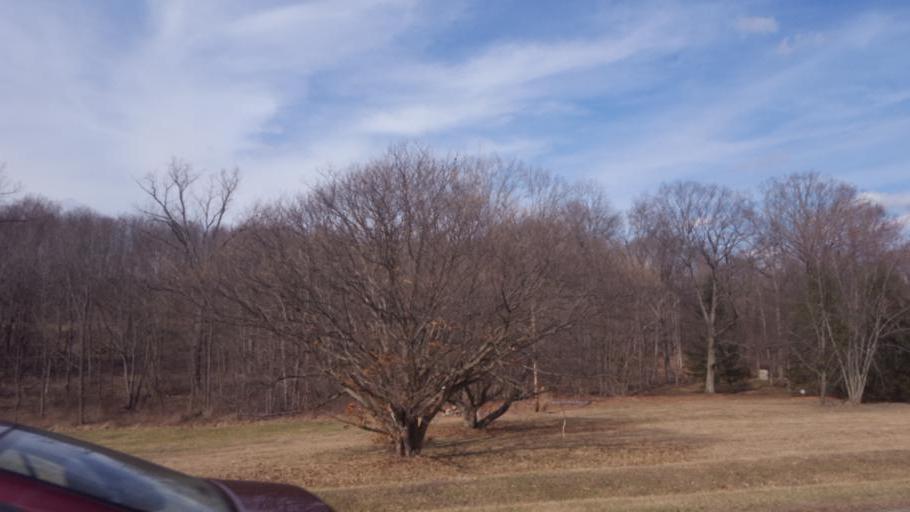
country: US
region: Ohio
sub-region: Knox County
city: Gambier
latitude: 40.4558
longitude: -82.4171
